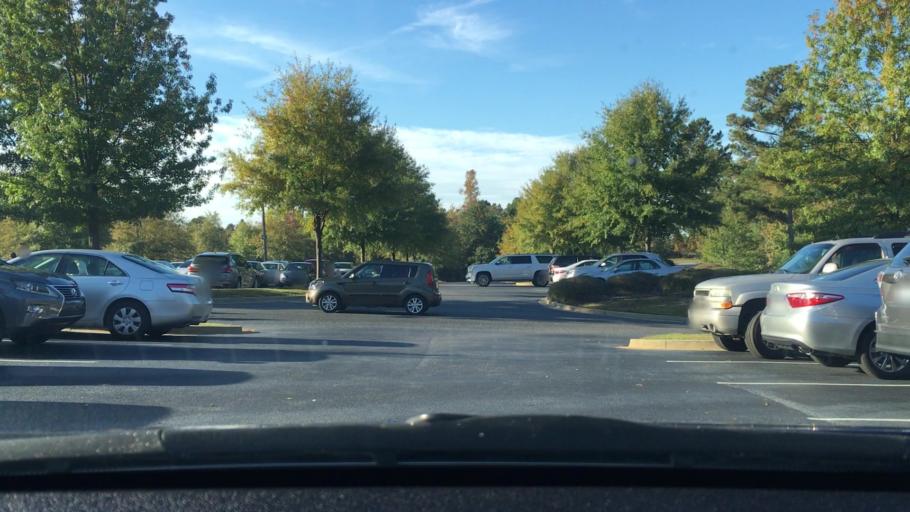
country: US
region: South Carolina
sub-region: Lexington County
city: Irmo
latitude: 34.0861
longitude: -81.1533
